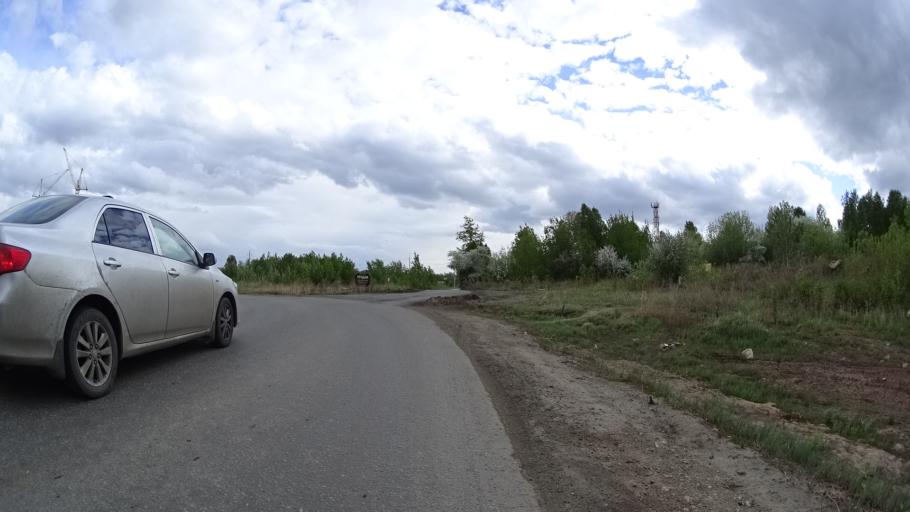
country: RU
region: Chelyabinsk
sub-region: Gorod Chelyabinsk
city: Chelyabinsk
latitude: 55.1601
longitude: 61.2856
